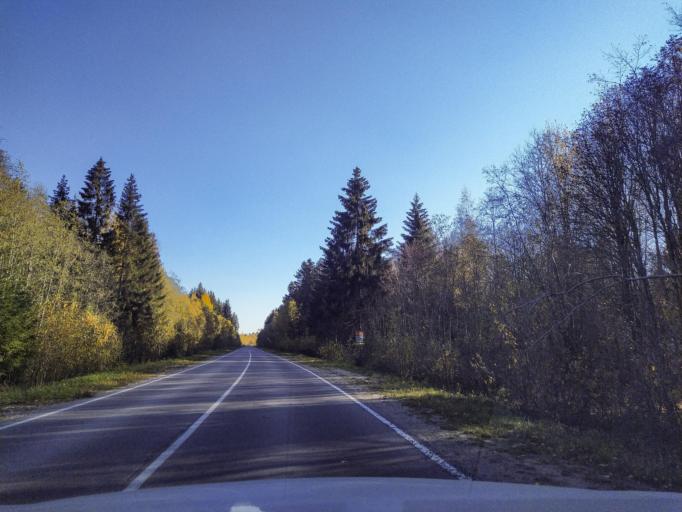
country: RU
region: Leningrad
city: Siverskiy
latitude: 59.3079
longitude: 30.0297
